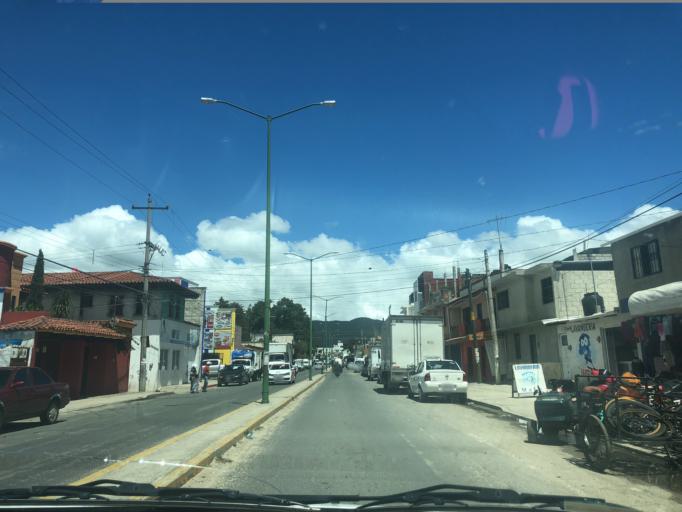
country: MX
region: Chiapas
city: San Cristobal de las Casas
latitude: 16.7192
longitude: -92.6400
